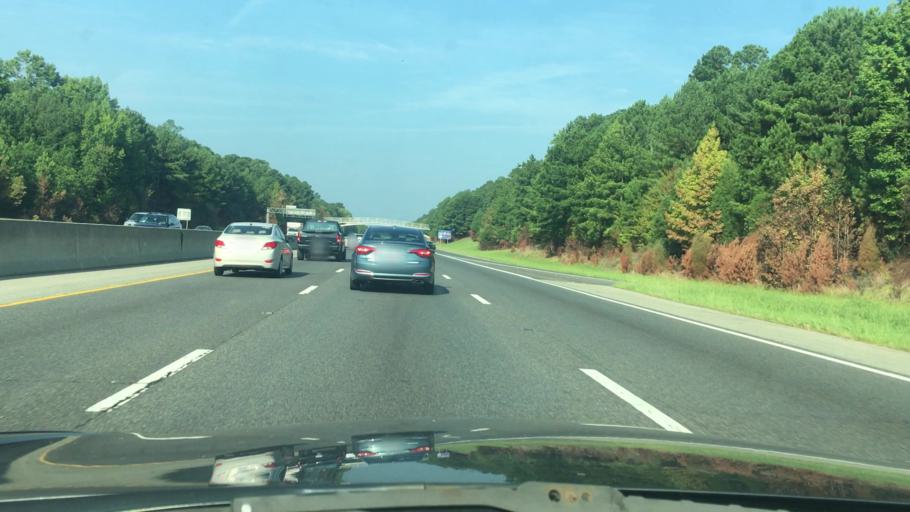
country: US
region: North Carolina
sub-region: Durham County
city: Durham
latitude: 35.9096
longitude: -78.9386
